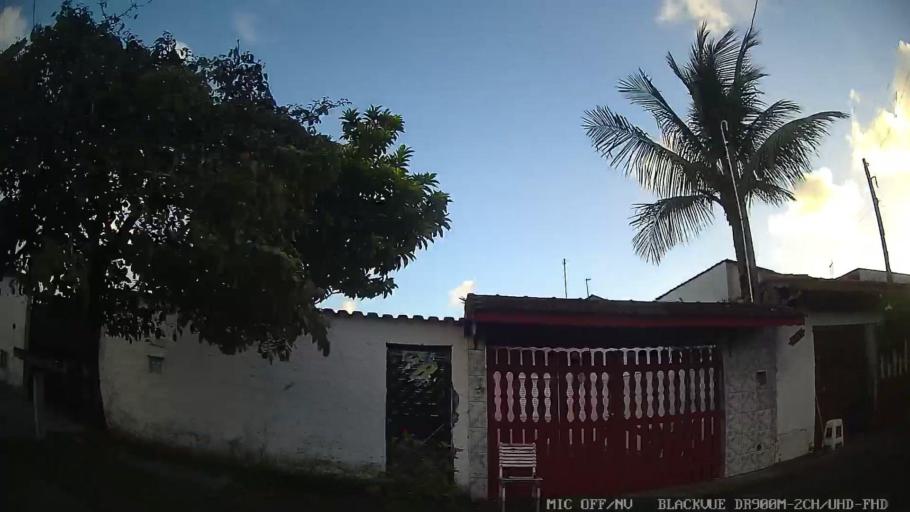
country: BR
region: Sao Paulo
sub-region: Itanhaem
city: Itanhaem
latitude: -24.1434
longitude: -46.7288
